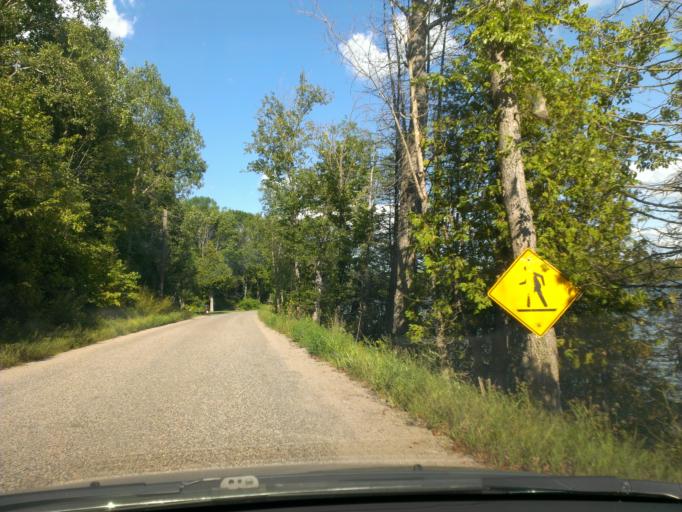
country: CA
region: Ontario
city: Skatepark
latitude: 44.7400
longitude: -76.9076
